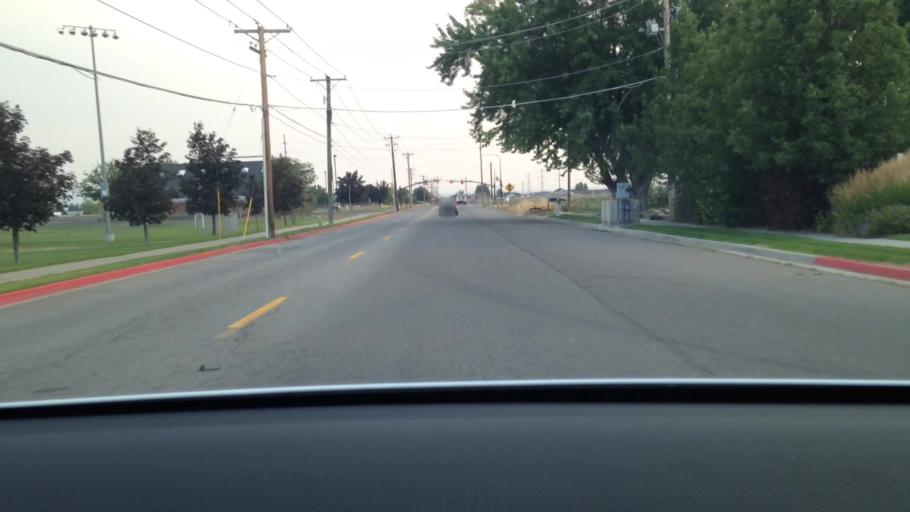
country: US
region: Utah
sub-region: Davis County
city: Layton
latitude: 41.0699
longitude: -112.0070
